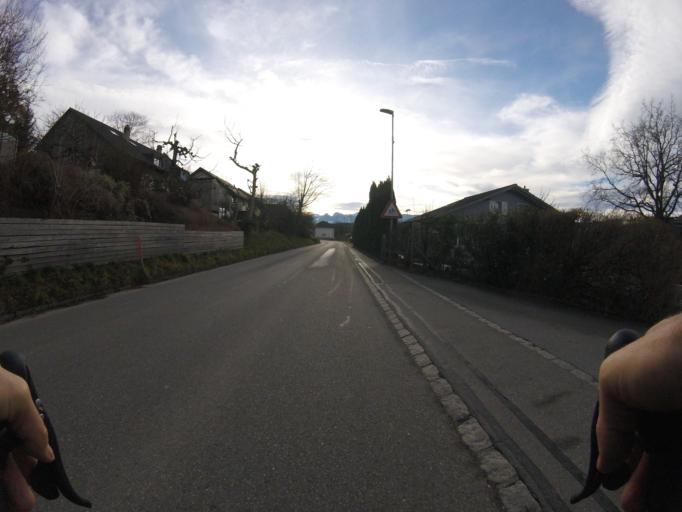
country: CH
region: Fribourg
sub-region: Sense District
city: Ueberstorf
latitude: 46.8537
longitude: 7.3158
